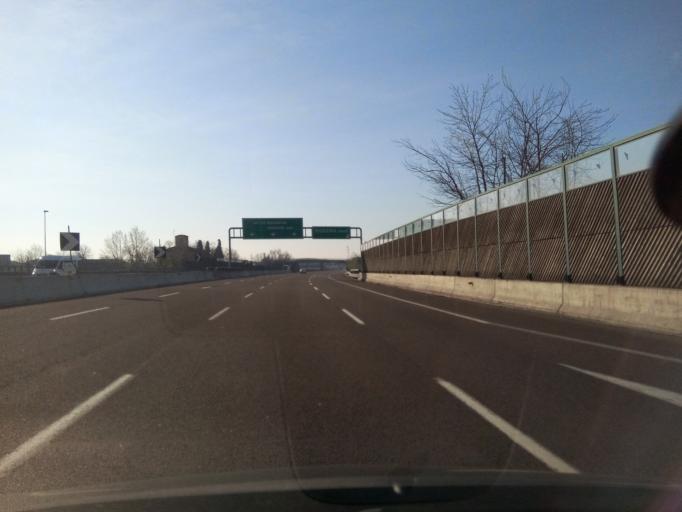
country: IT
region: Emilia-Romagna
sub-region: Provincia di Modena
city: Campogalliano
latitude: 44.6599
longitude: 10.8589
